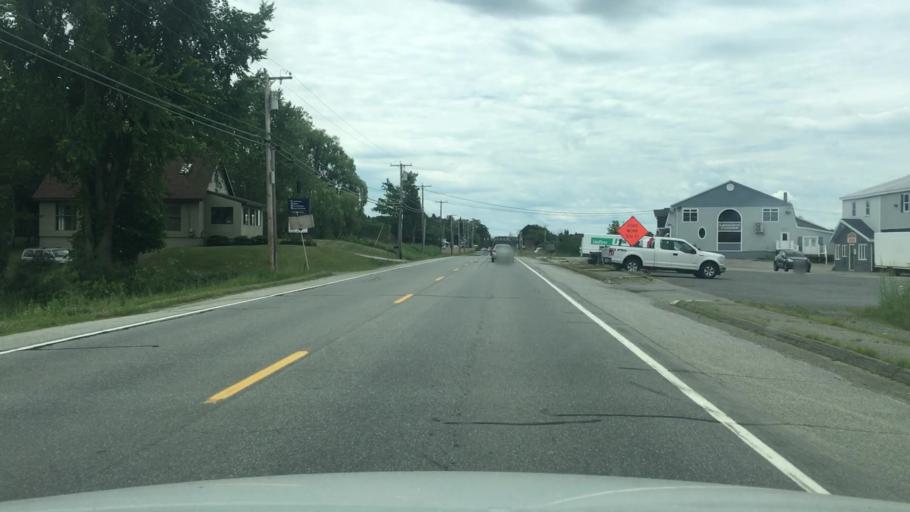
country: US
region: Maine
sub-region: Kennebec County
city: Augusta
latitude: 44.3303
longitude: -69.7276
